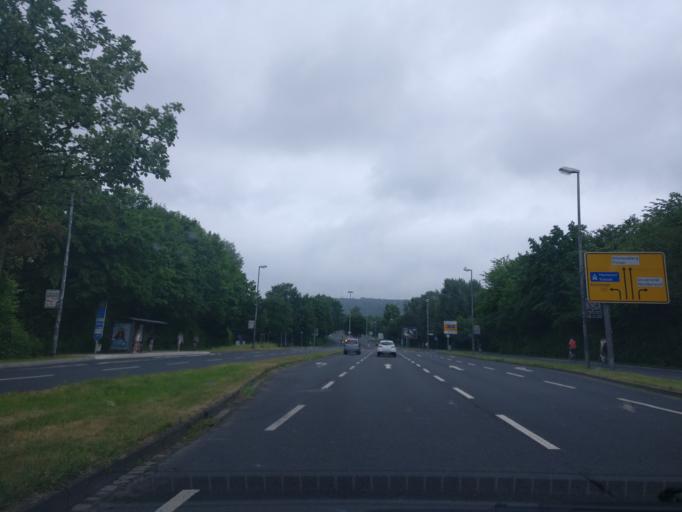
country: DE
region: Lower Saxony
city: Goettingen
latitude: 51.5567
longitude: 9.9428
